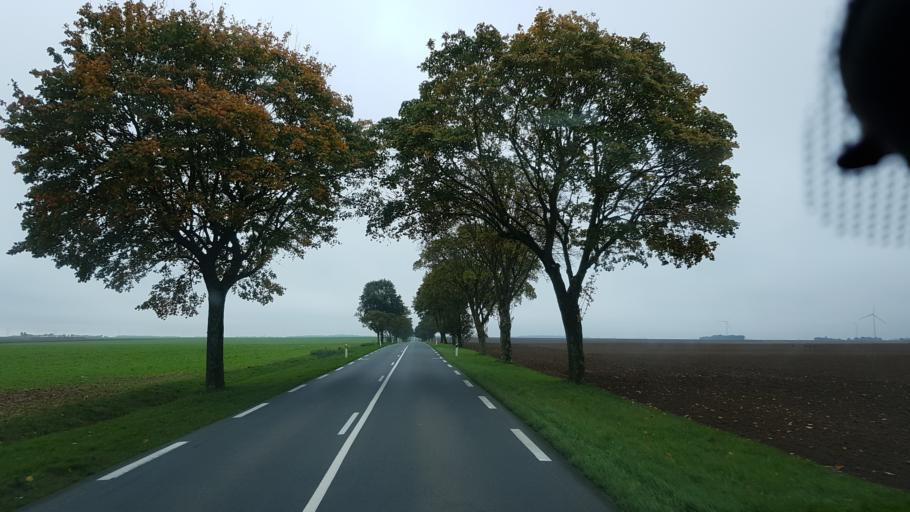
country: FR
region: Ile-de-France
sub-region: Departement de l'Essonne
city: Pussay
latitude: 48.3977
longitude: 1.9716
